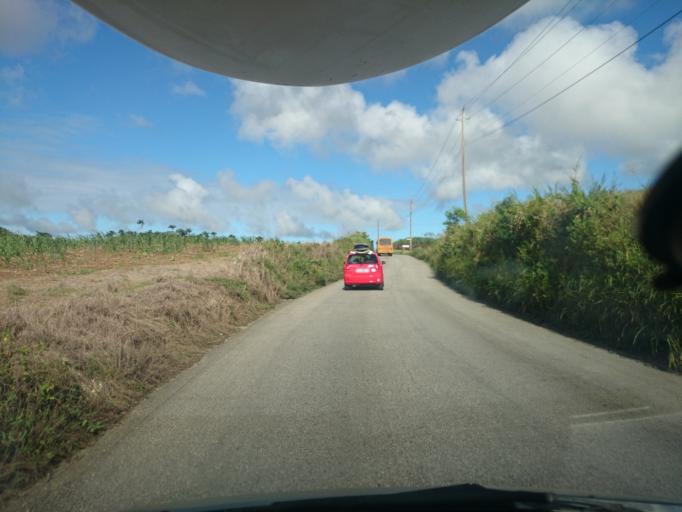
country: BB
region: Saint Thomas
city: Welchman Hall
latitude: 13.1648
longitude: -59.5547
